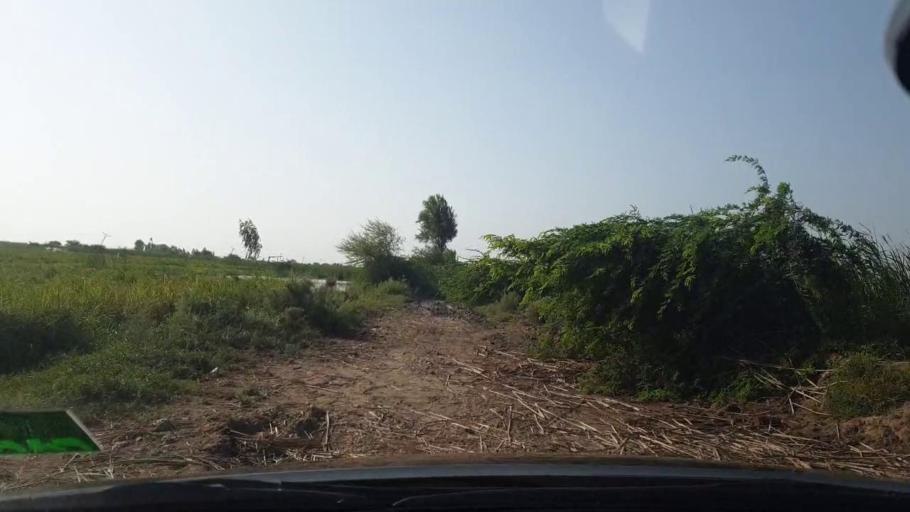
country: PK
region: Sindh
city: Tando Bago
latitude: 24.7066
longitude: 68.9554
